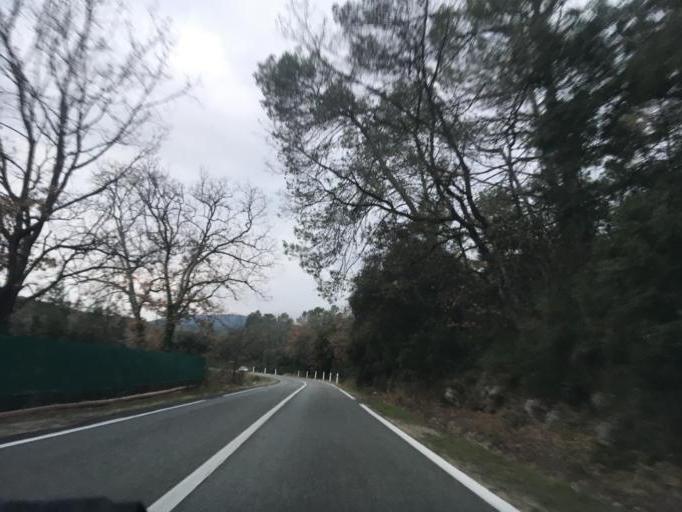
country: FR
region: Provence-Alpes-Cote d'Azur
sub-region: Departement du Var
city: Flassans-sur-Issole
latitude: 43.3614
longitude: 6.2009
